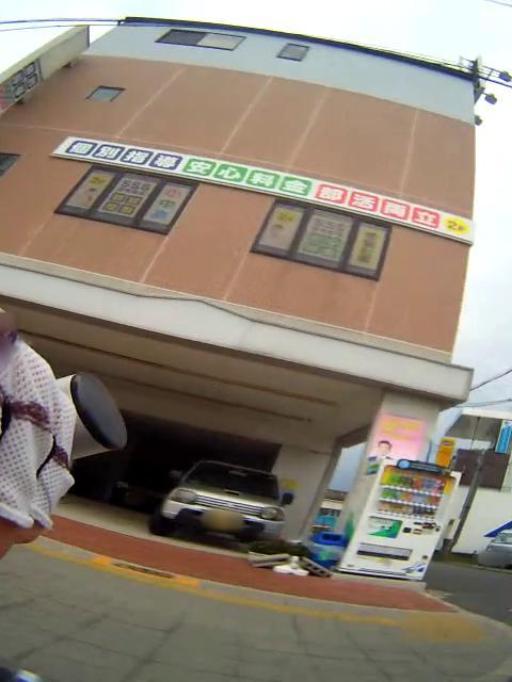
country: JP
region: Osaka
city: Moriguchi
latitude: 34.7186
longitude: 135.5696
